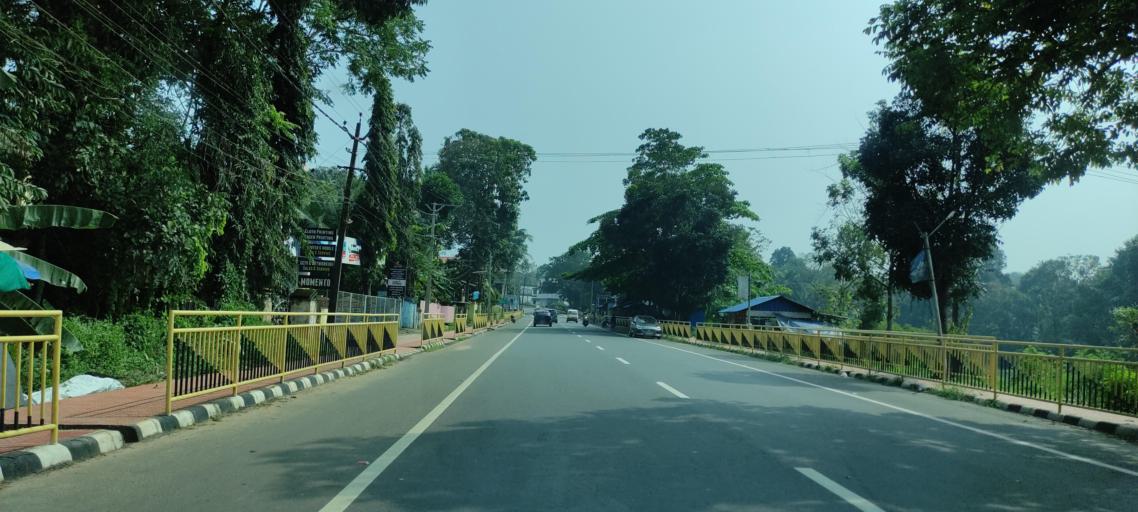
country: IN
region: Kerala
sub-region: Alappuzha
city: Chengannur
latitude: 9.2479
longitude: 76.6684
